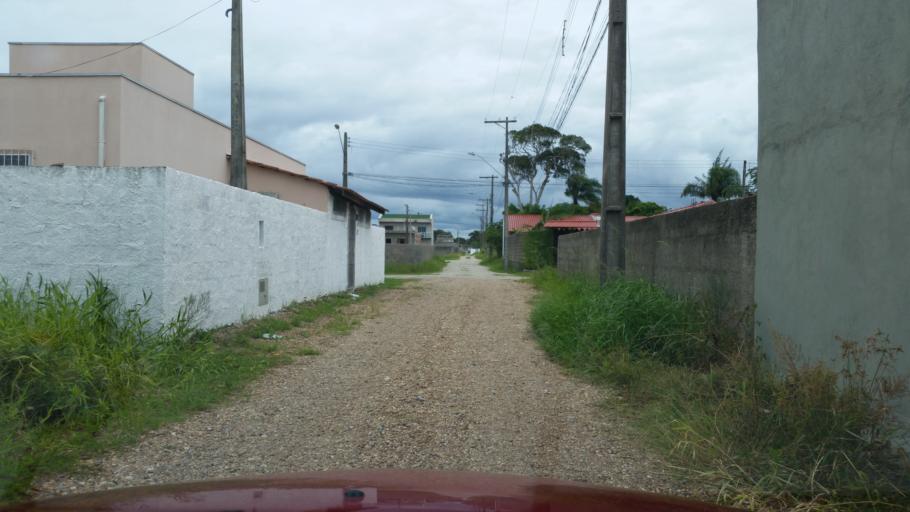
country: BR
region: Sao Paulo
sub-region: Iguape
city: Iguape
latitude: -24.7364
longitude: -47.5513
